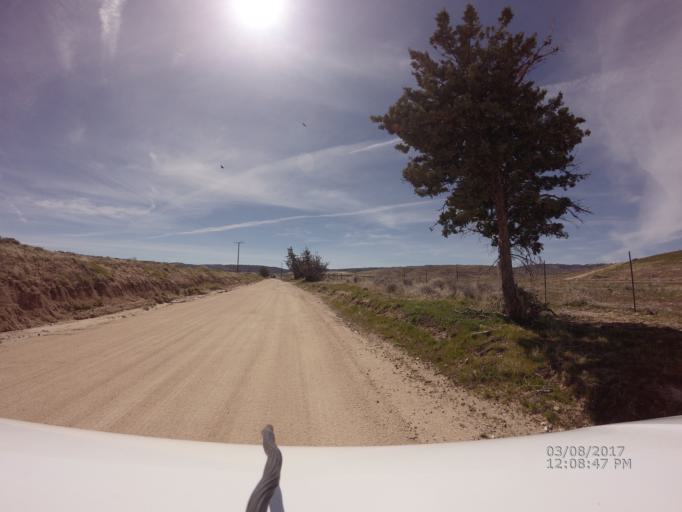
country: US
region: California
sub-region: Los Angeles County
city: Green Valley
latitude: 34.7317
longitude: -118.4284
